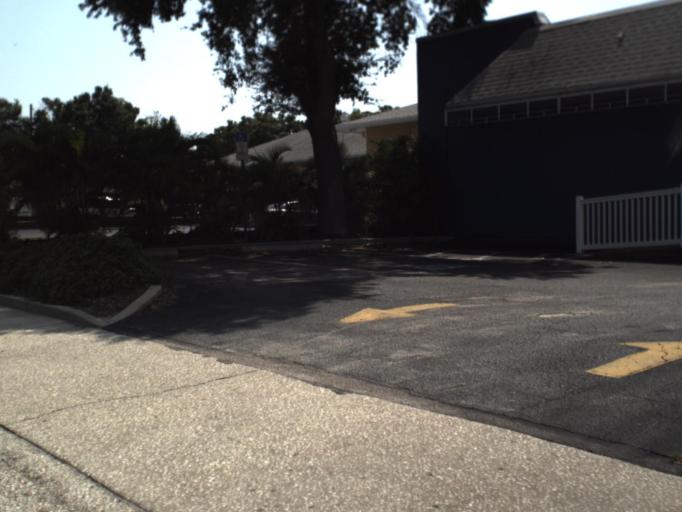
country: US
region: Florida
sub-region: Pinellas County
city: Kenneth City
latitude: 27.8237
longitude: -82.7286
